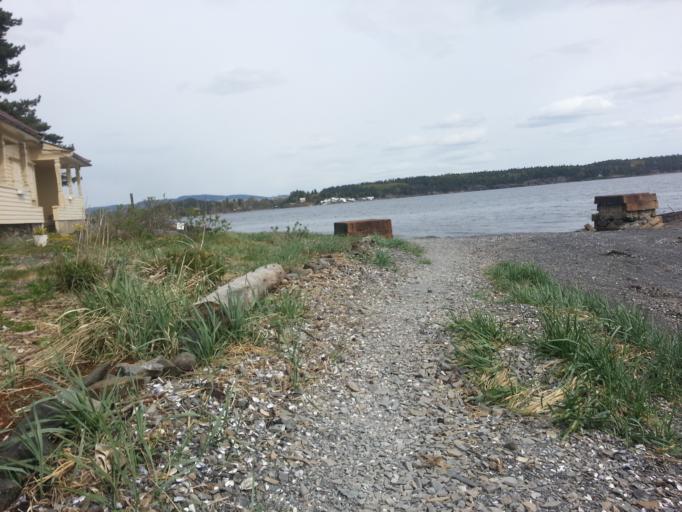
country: NO
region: Akershus
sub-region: Baerum
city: Lysaker
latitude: 59.9045
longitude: 10.6389
